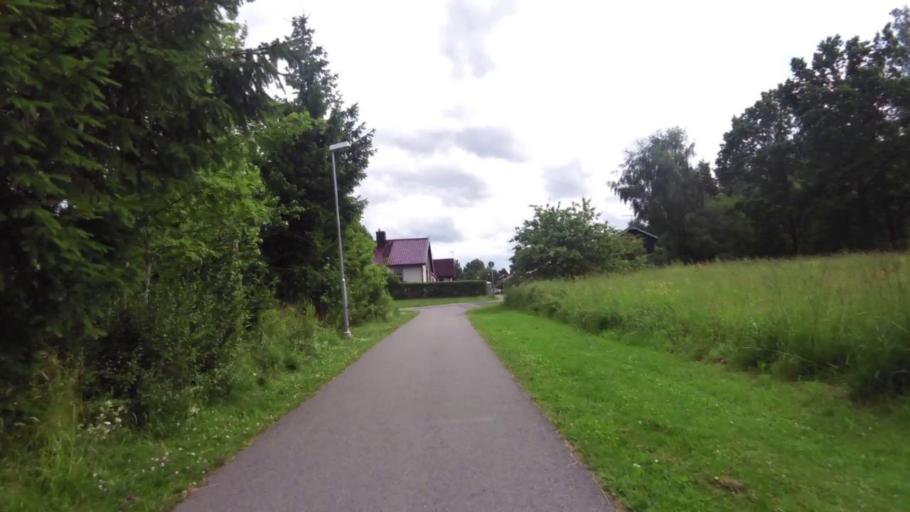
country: SE
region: OEstergoetland
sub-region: Linkopings Kommun
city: Malmslatt
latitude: 58.4153
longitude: 15.5585
